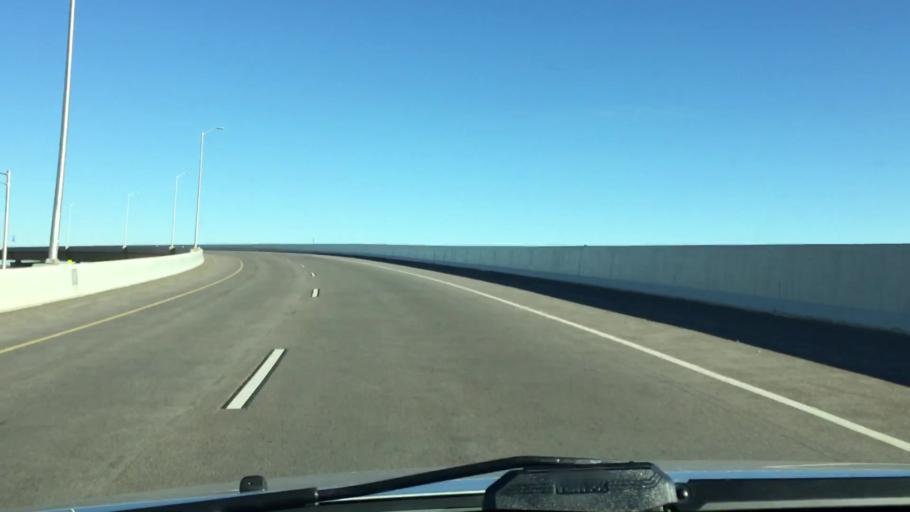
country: US
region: Wisconsin
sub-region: Brown County
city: Howard
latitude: 44.5359
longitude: -88.0787
